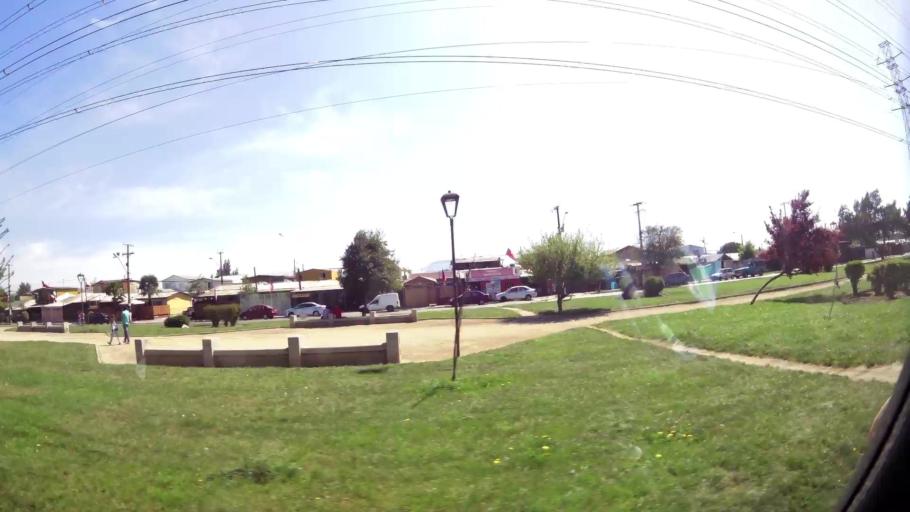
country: CL
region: Santiago Metropolitan
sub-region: Provincia de Santiago
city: Lo Prado
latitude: -33.4989
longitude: -70.7326
